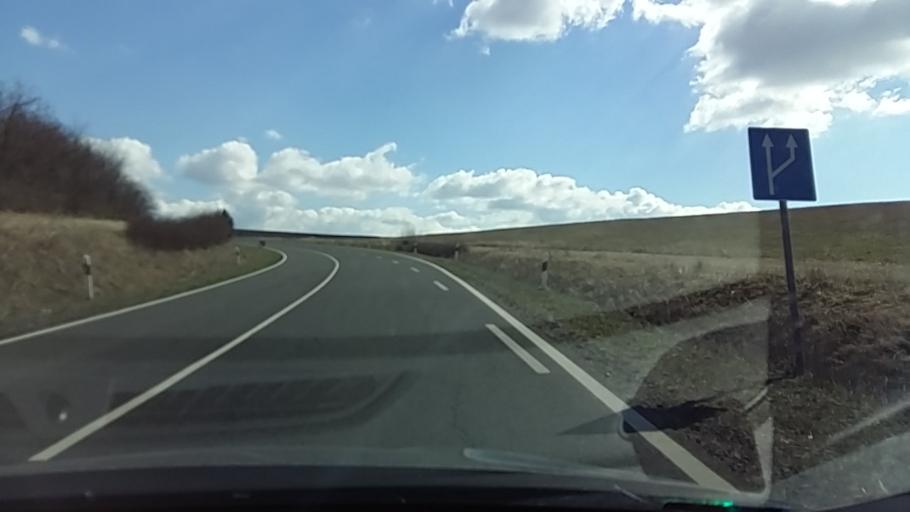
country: HU
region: Baranya
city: Kozarmisleny
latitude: 46.0242
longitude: 18.2807
